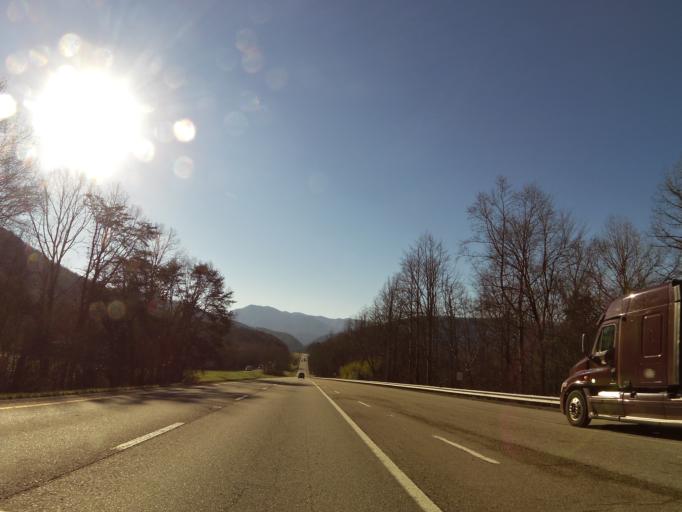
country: US
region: Tennessee
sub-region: Cocke County
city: Newport
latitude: 35.8625
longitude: -83.1848
